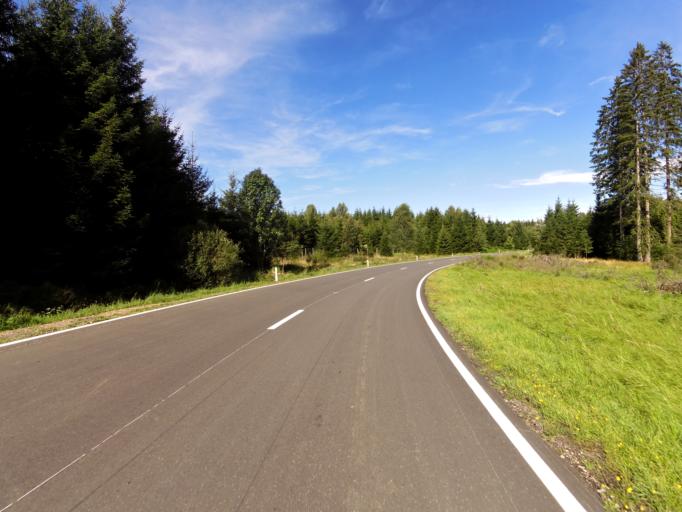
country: BE
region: Wallonia
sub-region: Province du Luxembourg
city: Tenneville
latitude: 50.1086
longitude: 5.4438
